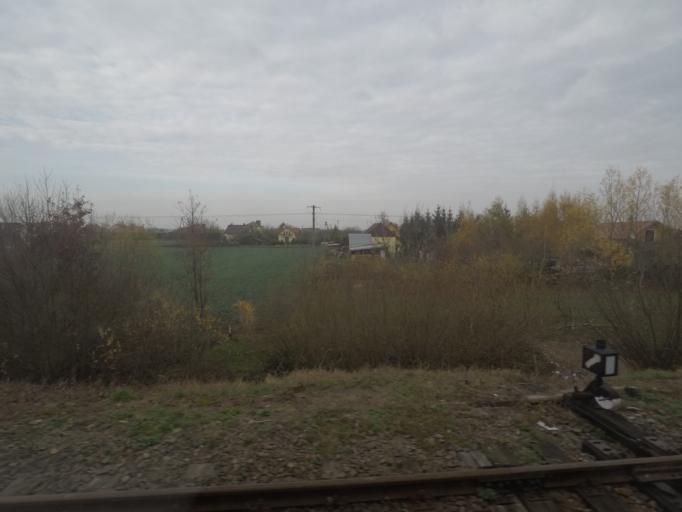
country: PL
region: Subcarpathian Voivodeship
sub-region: Powiat przemyski
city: Medyka
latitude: 49.7857
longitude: 22.8534
